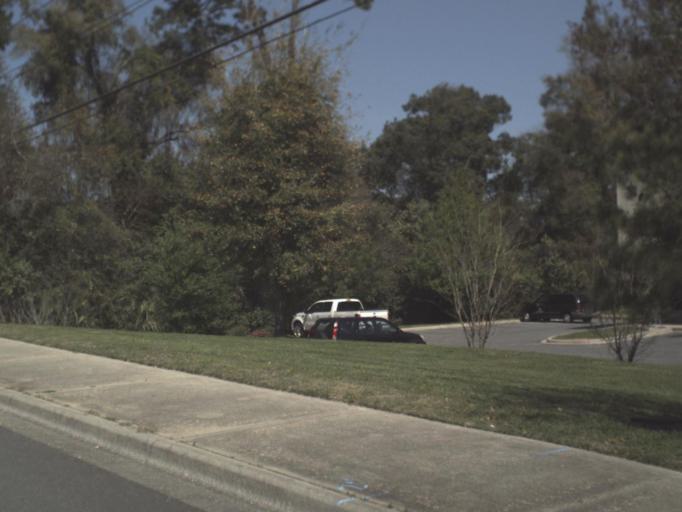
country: US
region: Florida
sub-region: Leon County
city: Tallahassee
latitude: 30.4013
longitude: -84.2805
